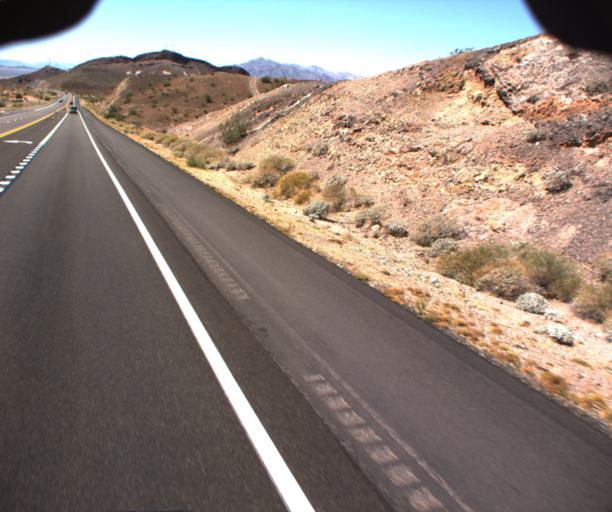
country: US
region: Arizona
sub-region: Mohave County
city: Desert Hills
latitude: 34.6113
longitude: -114.3538
